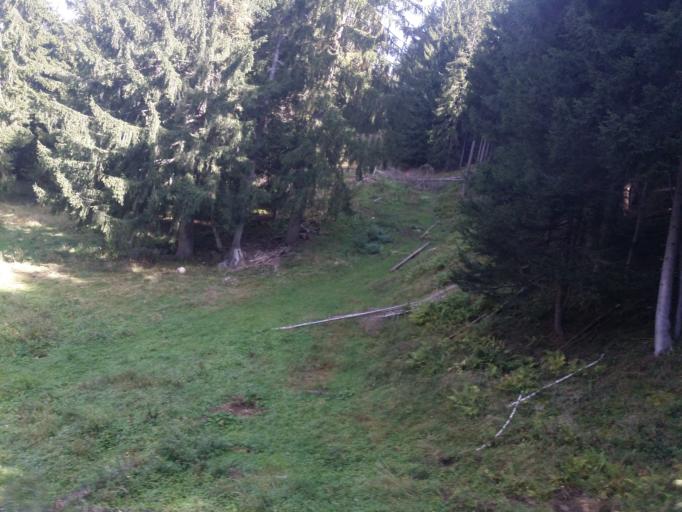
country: FR
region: Rhone-Alpes
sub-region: Departement de la Haute-Savoie
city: Chamonix-Mont-Blanc
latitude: 45.9297
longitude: 6.8906
